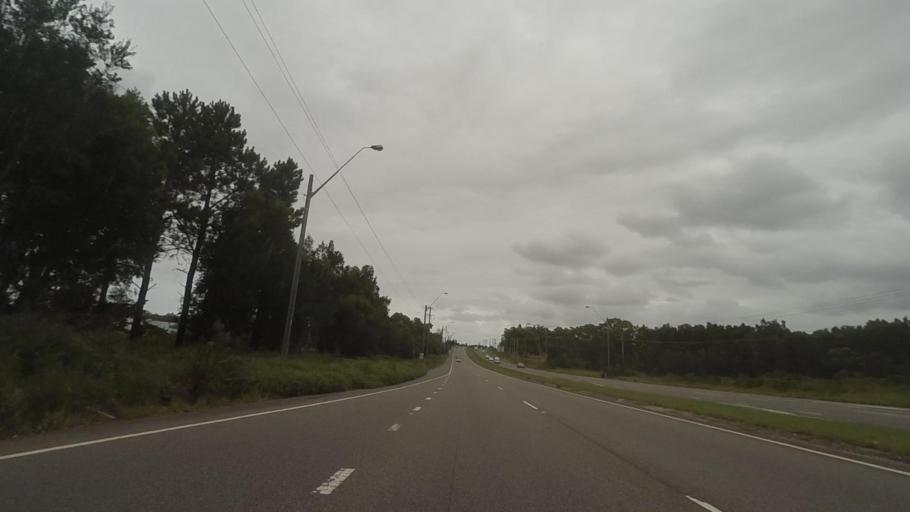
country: AU
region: New South Wales
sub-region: Wyong Shire
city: Buff Point
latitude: -33.2001
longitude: 151.5223
